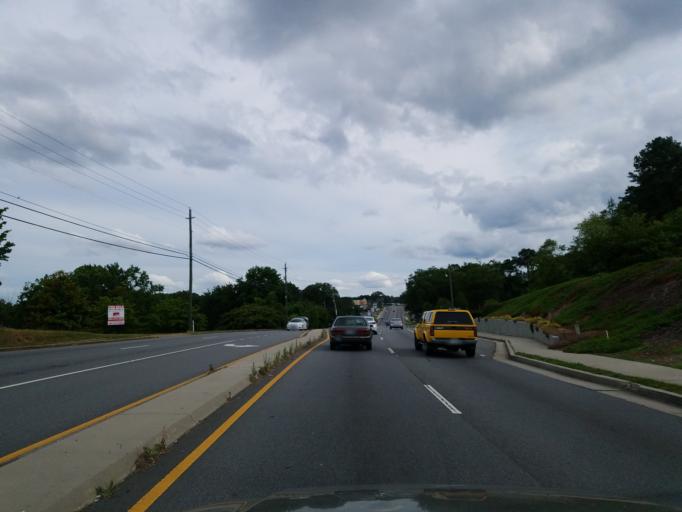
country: US
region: Georgia
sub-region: Cobb County
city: Marietta
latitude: 34.0164
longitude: -84.5273
